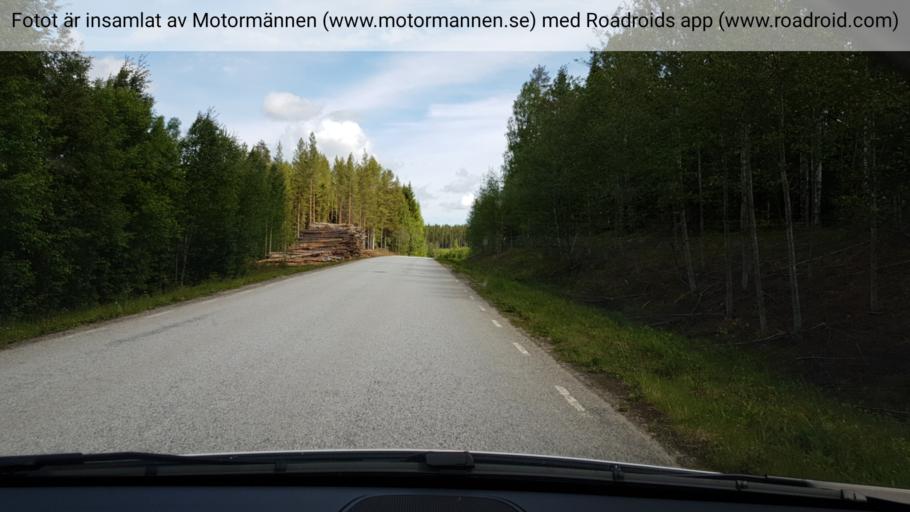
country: SE
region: Vaesterbotten
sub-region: Vannas Kommun
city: Vannasby
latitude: 64.0091
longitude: 19.9234
